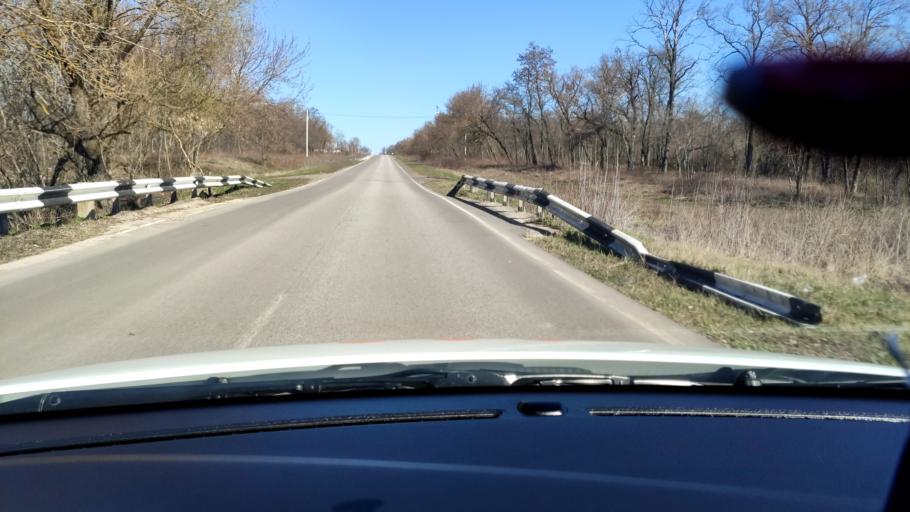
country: RU
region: Voronezj
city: Ramon'
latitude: 51.9771
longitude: 39.2245
